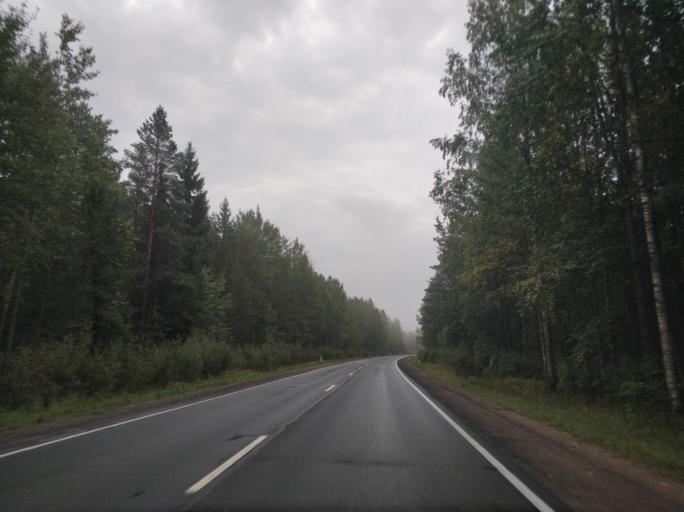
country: RU
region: Leningrad
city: Shcheglovo
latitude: 60.0992
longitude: 30.8380
